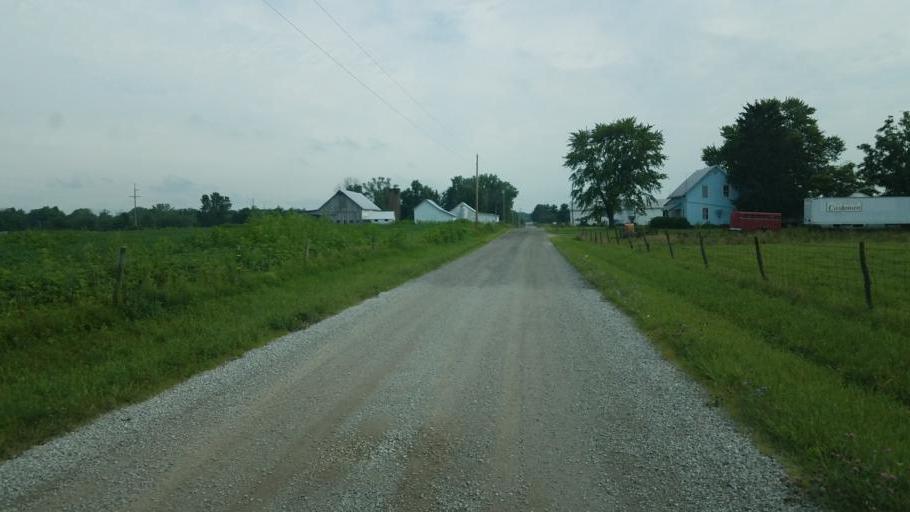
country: US
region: Ohio
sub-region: Delaware County
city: Ashley
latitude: 40.3893
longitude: -82.9118
